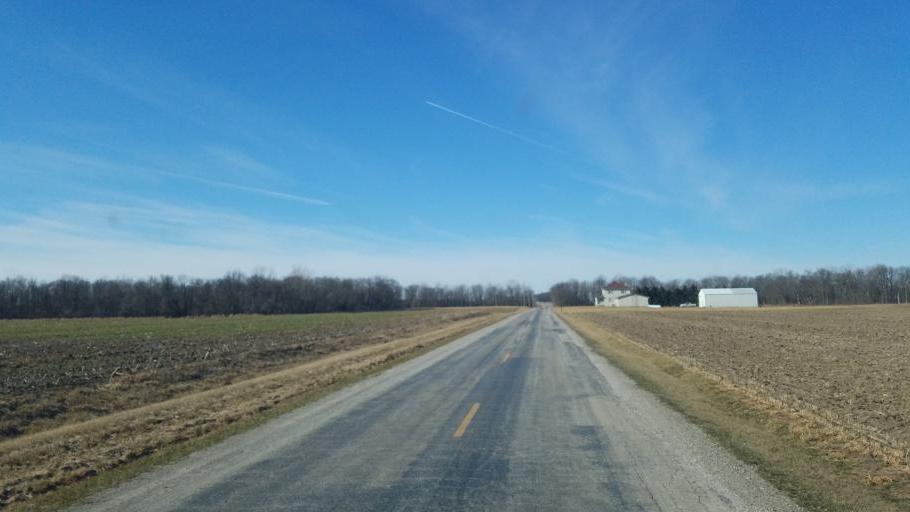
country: US
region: Ohio
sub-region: Union County
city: Richwood
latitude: 40.5257
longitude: -83.3333
